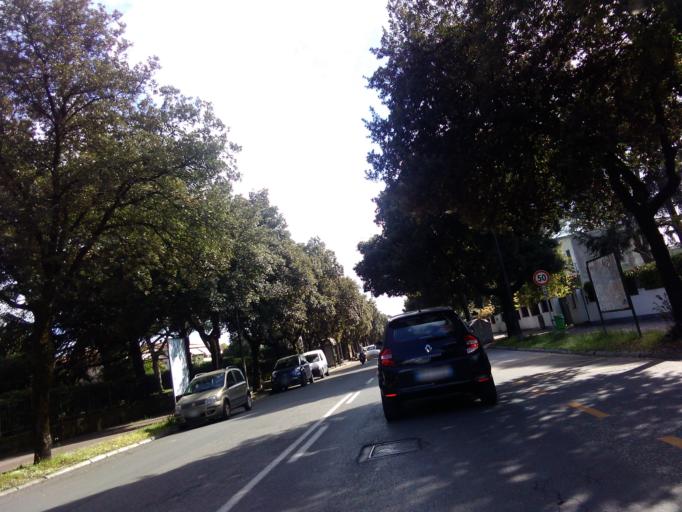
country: IT
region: Tuscany
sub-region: Provincia di Massa-Carrara
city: Massa
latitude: 44.0199
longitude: 10.1240
